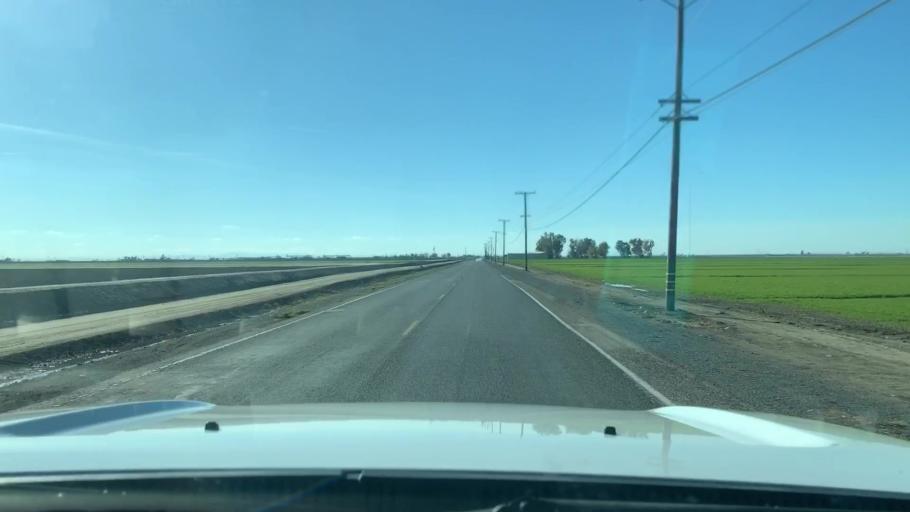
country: US
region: California
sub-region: Tulare County
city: Tulare
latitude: 36.1818
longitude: -119.3862
